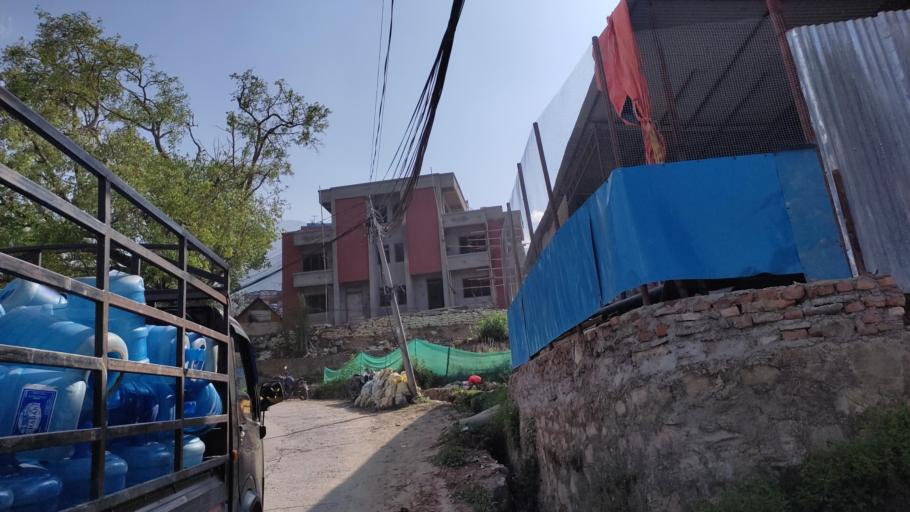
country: NP
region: Central Region
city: Kirtipur
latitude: 27.6732
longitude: 85.2517
